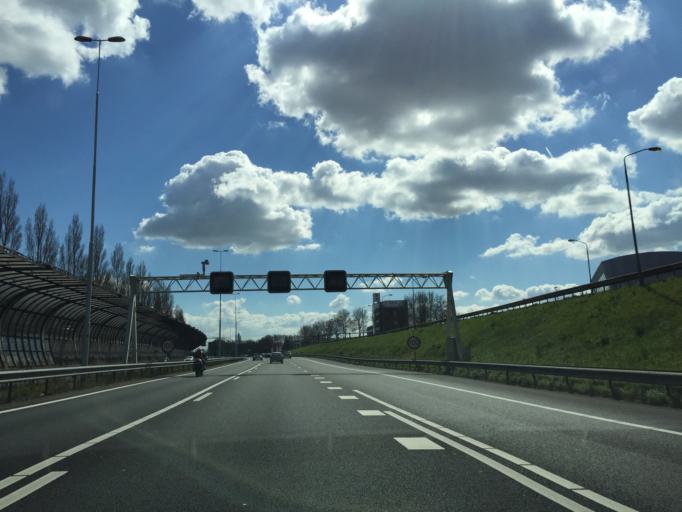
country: NL
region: South Holland
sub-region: Gemeente Zwijndrecht
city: Zwijndrecht
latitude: 51.7938
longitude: 4.6489
